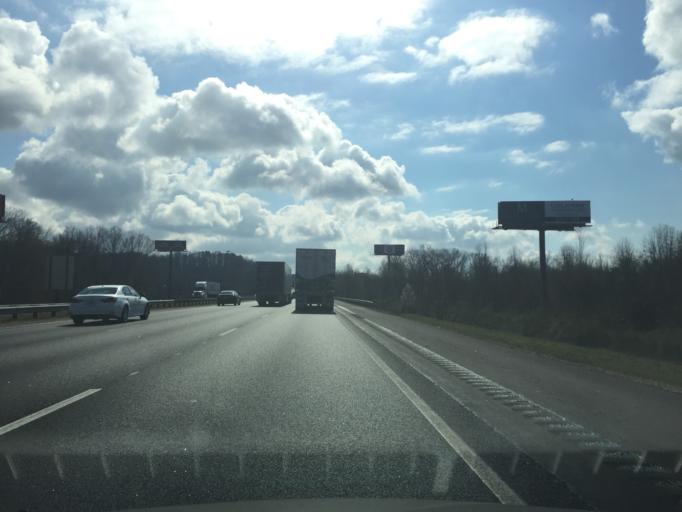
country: US
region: Georgia
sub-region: Catoosa County
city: Indian Springs
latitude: 34.9822
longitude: -85.2000
